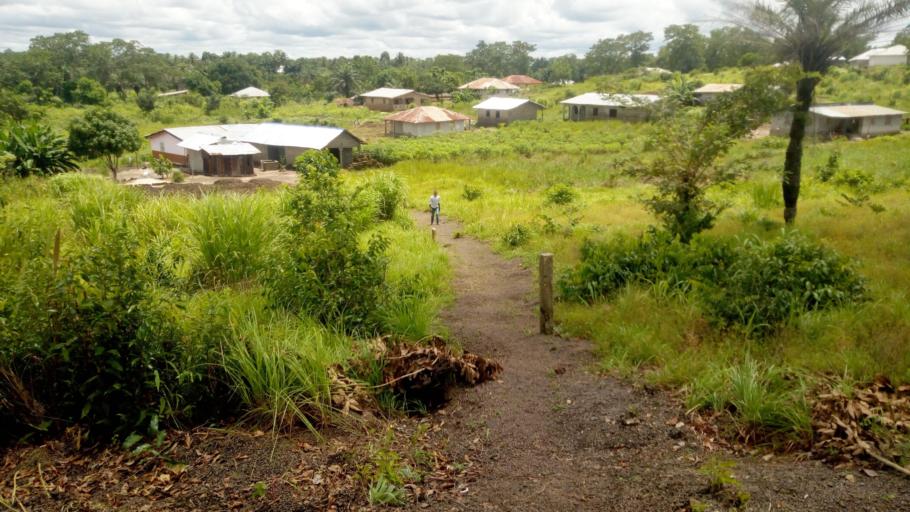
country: SL
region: Northern Province
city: Magburaka
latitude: 8.7107
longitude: -11.9552
